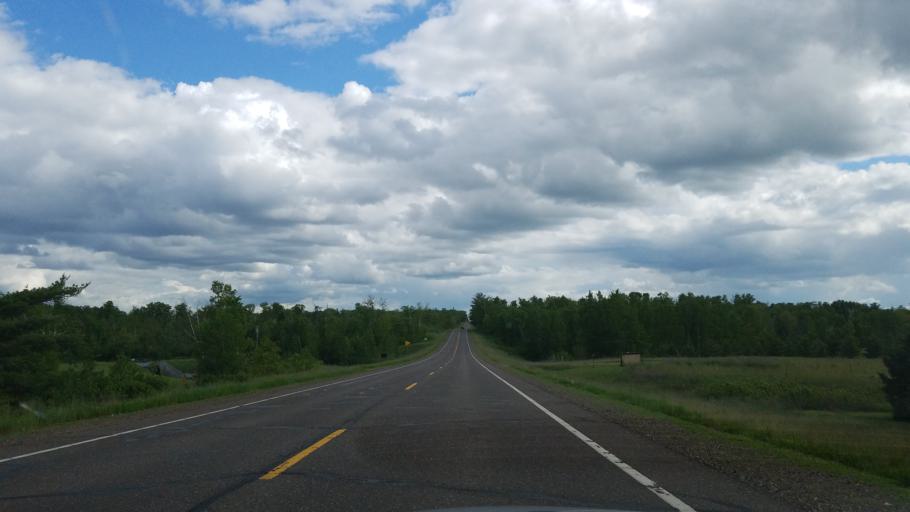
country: US
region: Wisconsin
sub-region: Burnett County
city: Siren
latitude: 46.1284
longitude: -92.2381
